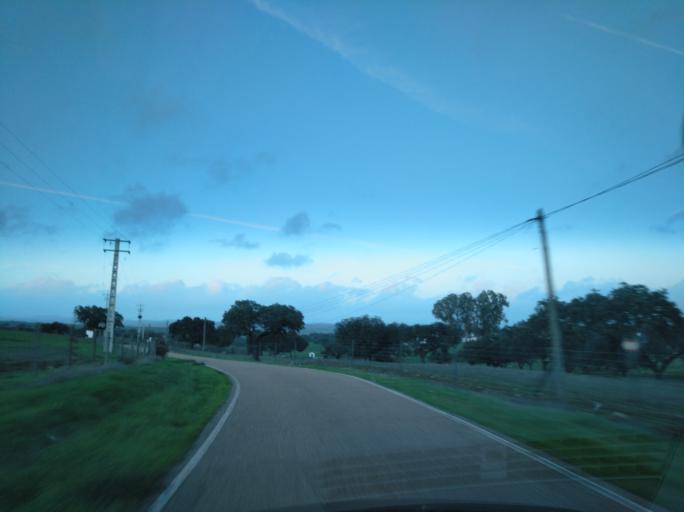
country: PT
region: Portalegre
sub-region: Campo Maior
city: Campo Maior
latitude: 39.0741
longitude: -7.1152
